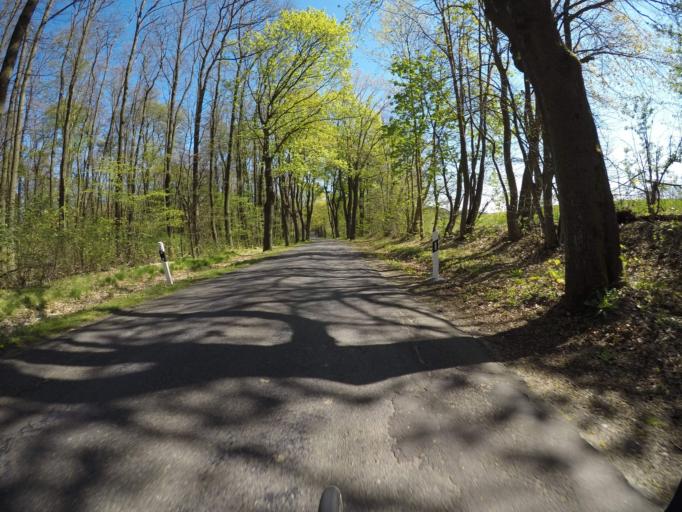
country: DE
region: Brandenburg
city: Werftpfuhl
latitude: 52.6222
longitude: 13.8233
